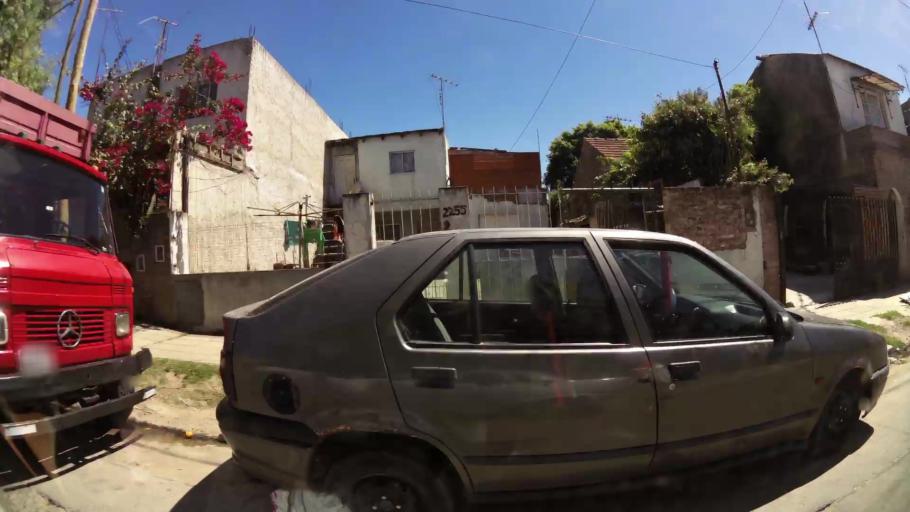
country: AR
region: Buenos Aires
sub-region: Partido de Tigre
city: Tigre
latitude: -34.4974
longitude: -58.5887
